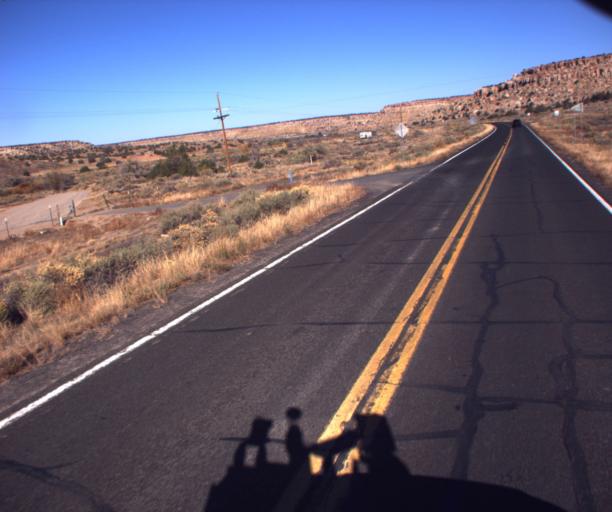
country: US
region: Arizona
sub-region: Navajo County
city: First Mesa
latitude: 35.8256
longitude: -110.2208
